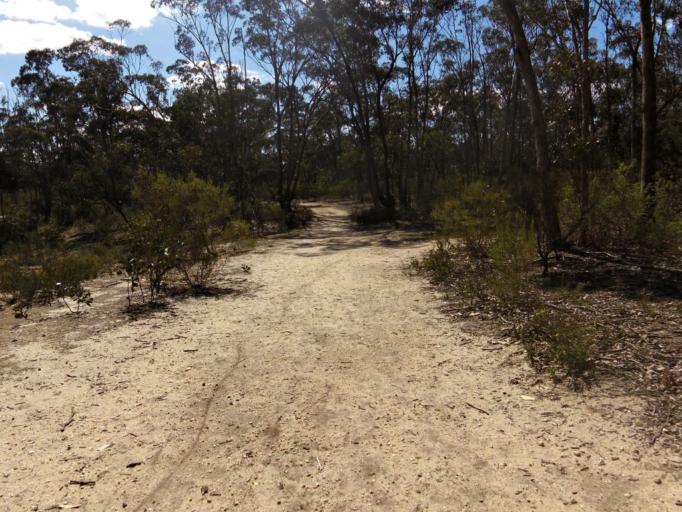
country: AU
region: Victoria
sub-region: Melton
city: Melton West
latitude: -37.6616
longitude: 144.5075
